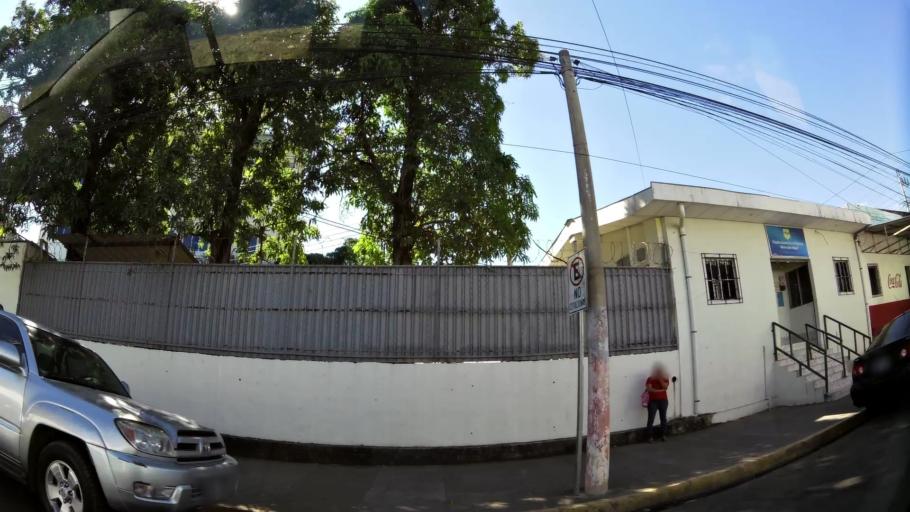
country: SV
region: San Miguel
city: San Miguel
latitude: 13.4736
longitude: -88.1710
